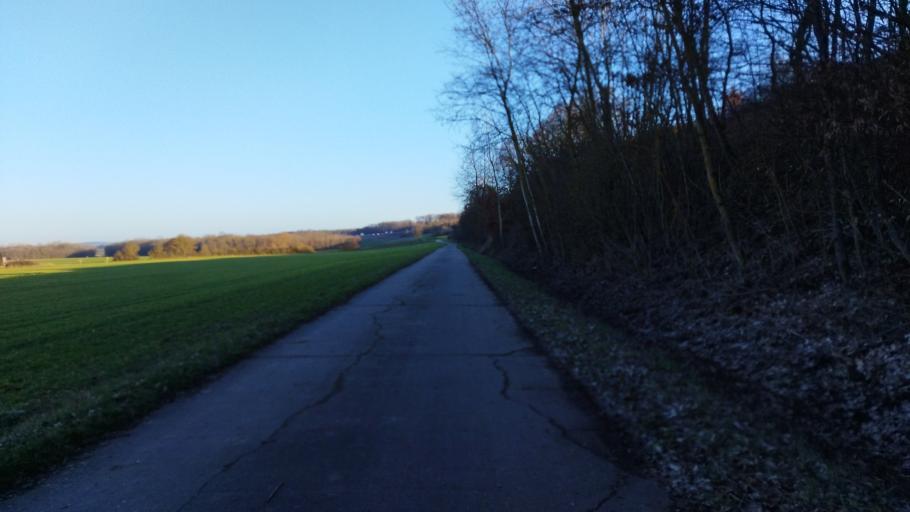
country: DE
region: Bavaria
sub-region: Regierungsbezirk Unterfranken
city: Dettelbach
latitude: 49.7895
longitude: 10.1887
